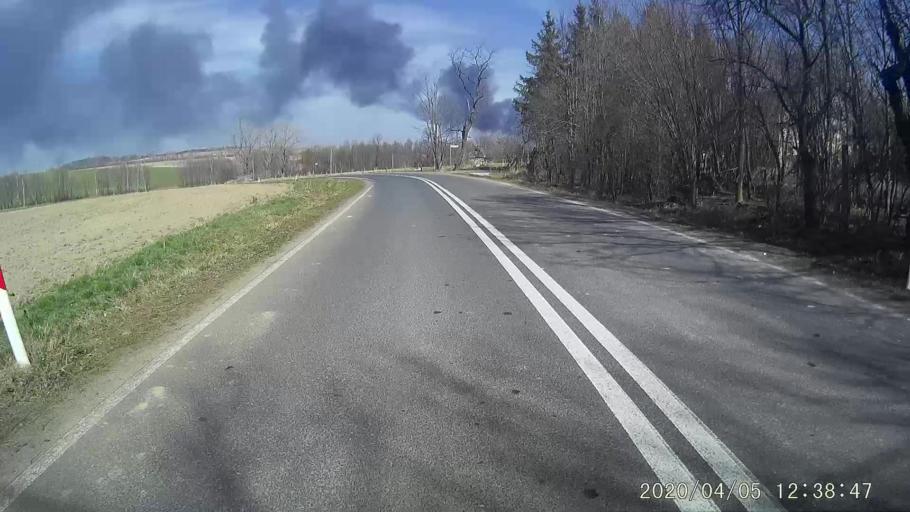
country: PL
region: Lower Silesian Voivodeship
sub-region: Powiat lwowecki
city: Mirsk
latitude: 51.0012
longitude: 15.3542
